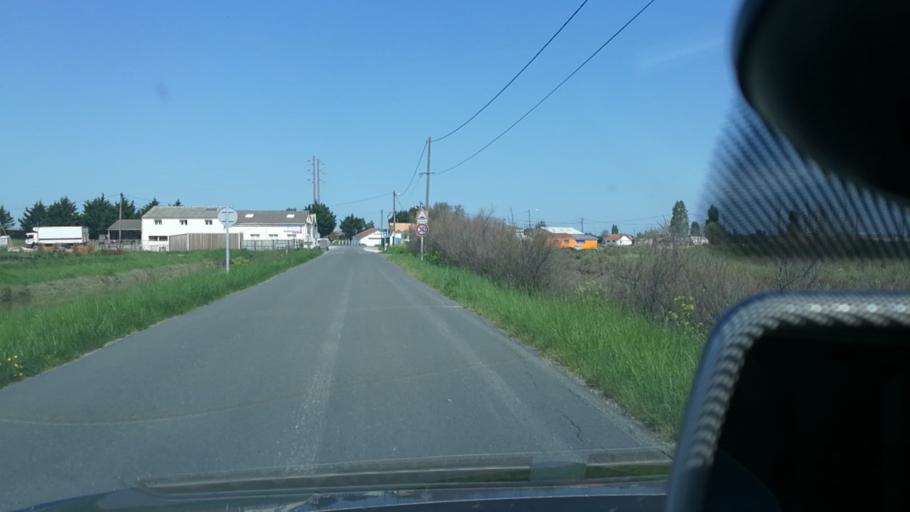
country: FR
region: Poitou-Charentes
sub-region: Departement de la Charente-Maritime
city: Saint-Trojan-les-Bains
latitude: 45.8693
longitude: -1.2196
